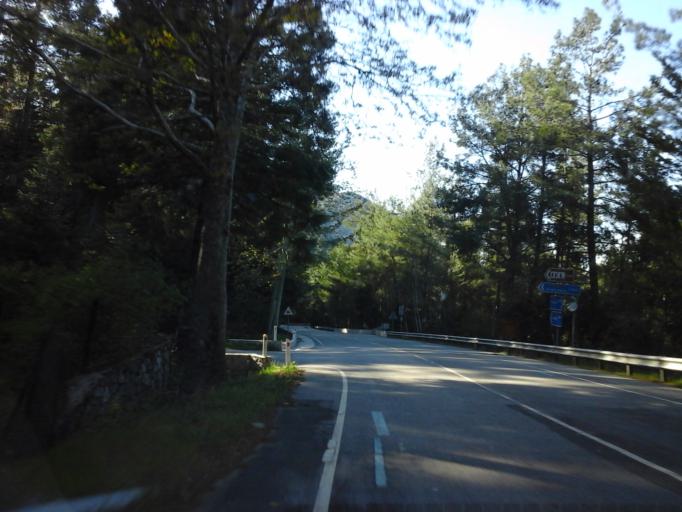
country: CY
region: Lefkosia
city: Kakopetria
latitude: 34.9493
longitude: 32.9281
